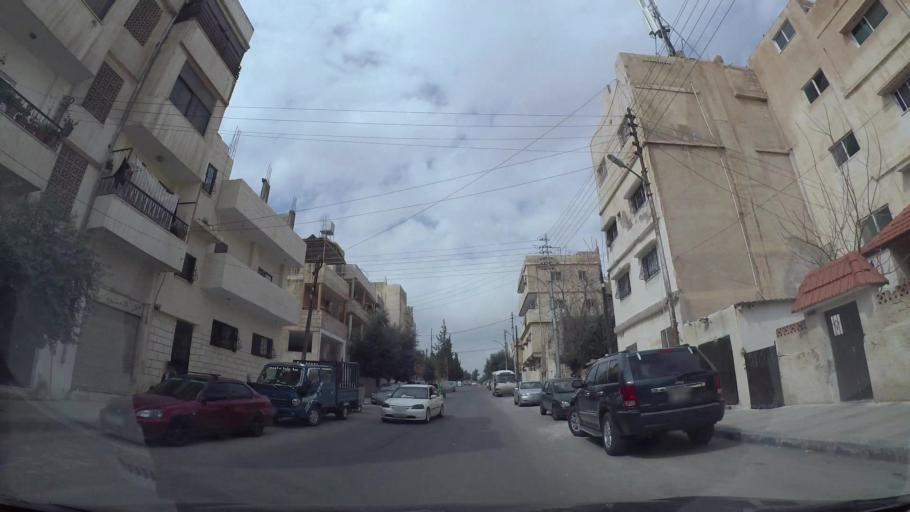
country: JO
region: Amman
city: Amman
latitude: 31.9624
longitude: 35.9524
